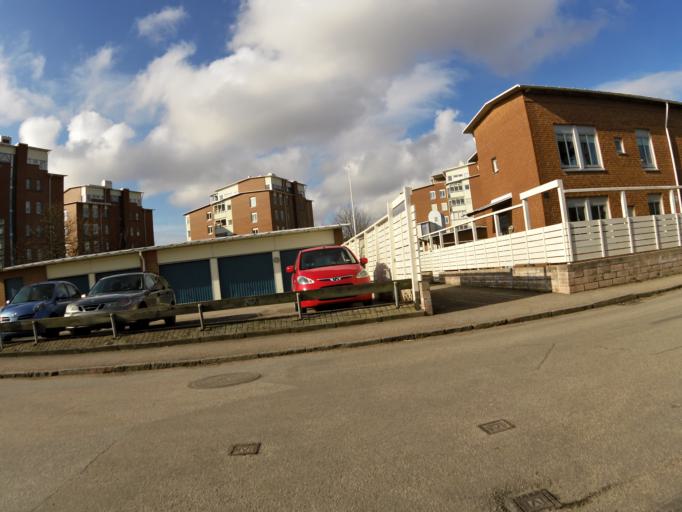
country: SE
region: Halland
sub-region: Halmstads Kommun
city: Halmstad
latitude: 56.6793
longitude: 12.8671
